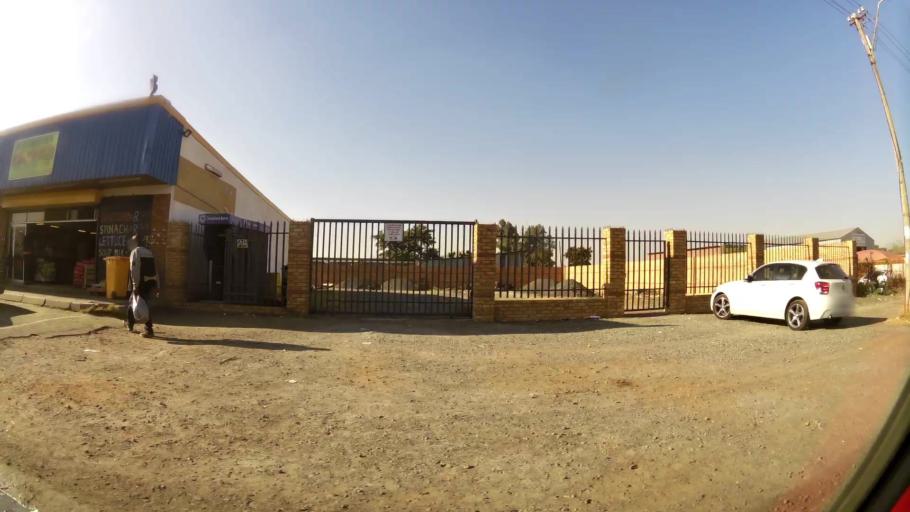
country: ZA
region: North-West
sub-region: Bojanala Platinum District Municipality
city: Rustenburg
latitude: -25.6541
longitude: 27.2353
